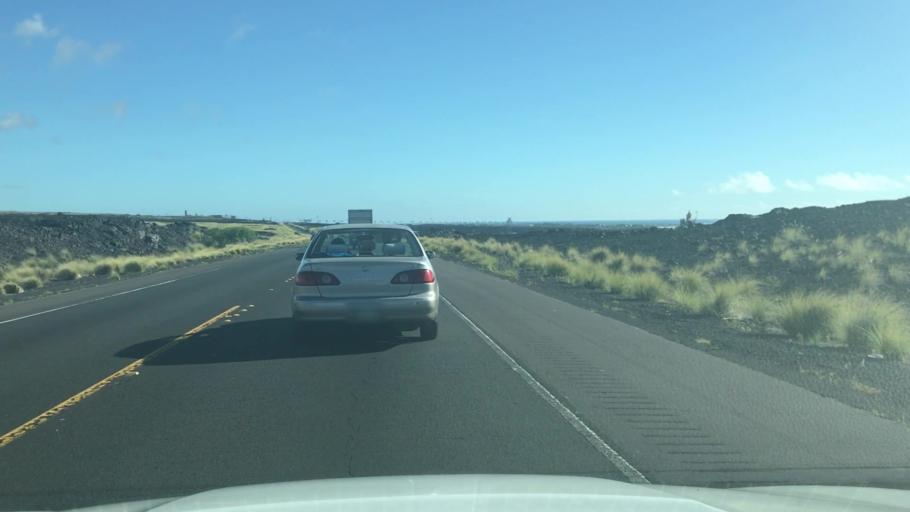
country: US
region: Hawaii
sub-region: Hawaii County
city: Kalaoa
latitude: 19.7606
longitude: -156.0252
